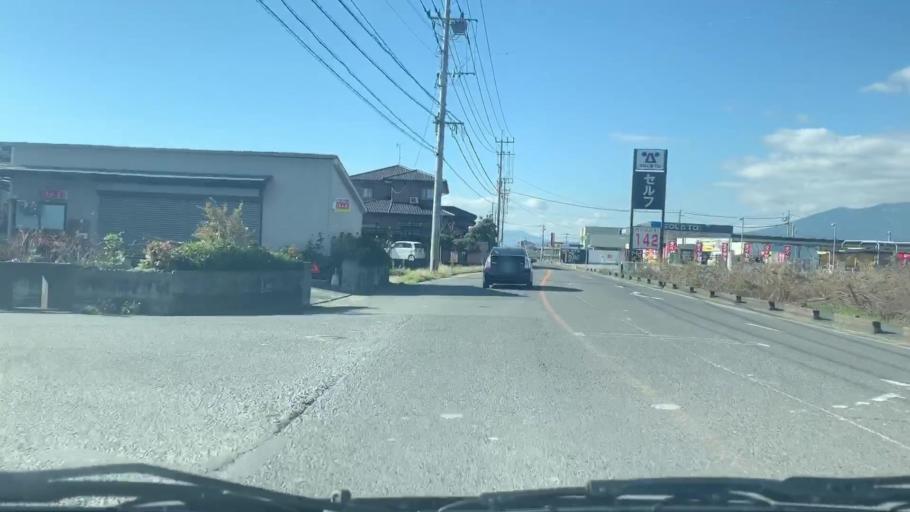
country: JP
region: Saga Prefecture
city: Saga-shi
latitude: 33.2907
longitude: 130.2788
